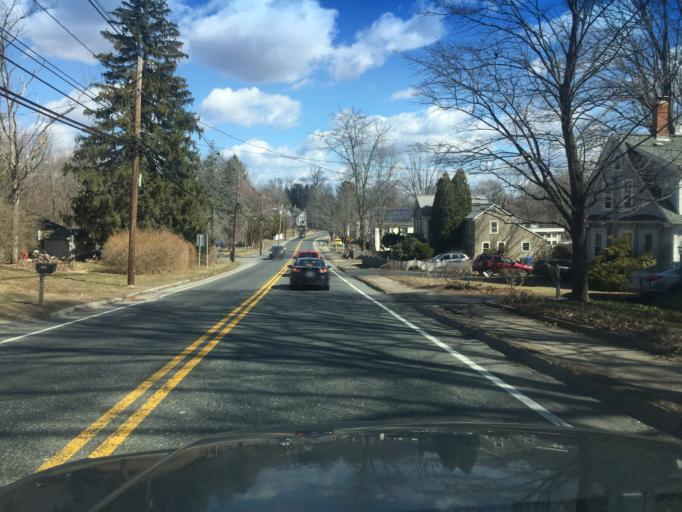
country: US
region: Massachusetts
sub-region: Middlesex County
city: Holliston
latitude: 42.1937
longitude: -71.4356
